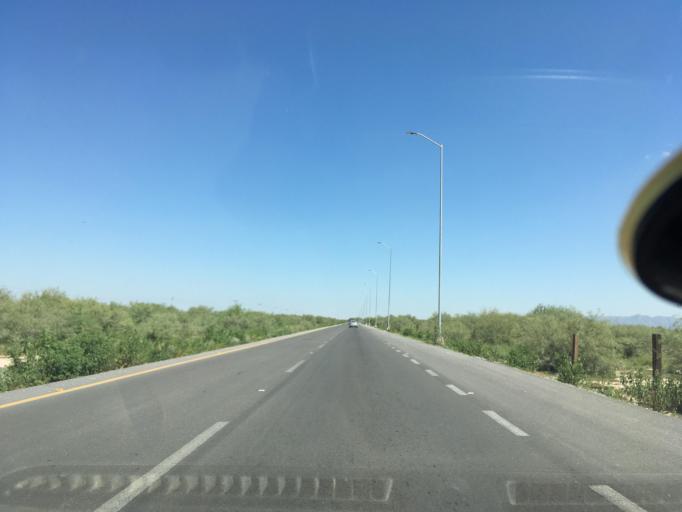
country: MX
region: Coahuila
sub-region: Torreon
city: Fraccionamiento la Noria
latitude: 25.4804
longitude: -103.3197
